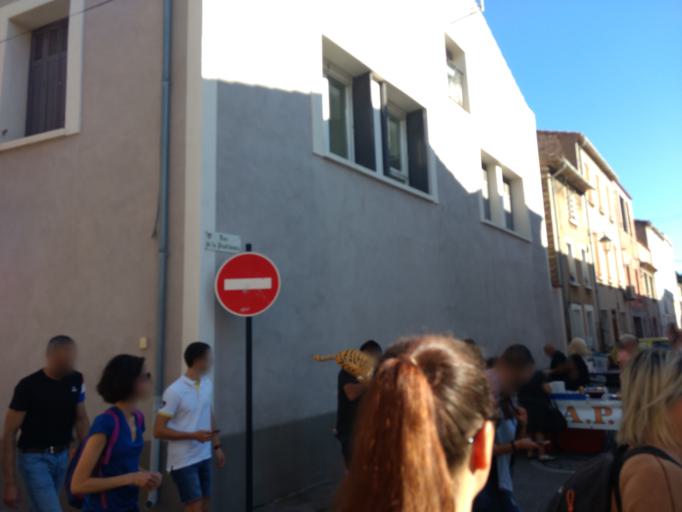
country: FR
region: Languedoc-Roussillon
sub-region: Departement de l'Aude
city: Leucate
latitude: 42.9100
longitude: 3.0290
